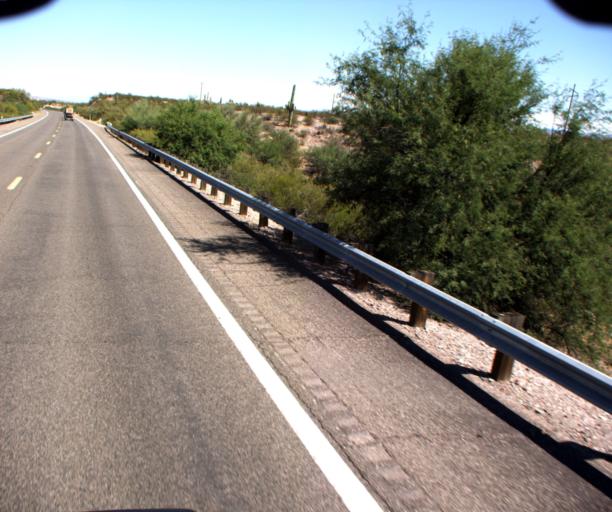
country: US
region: Arizona
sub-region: Pinal County
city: Mammoth
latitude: 32.8113
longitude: -110.6858
